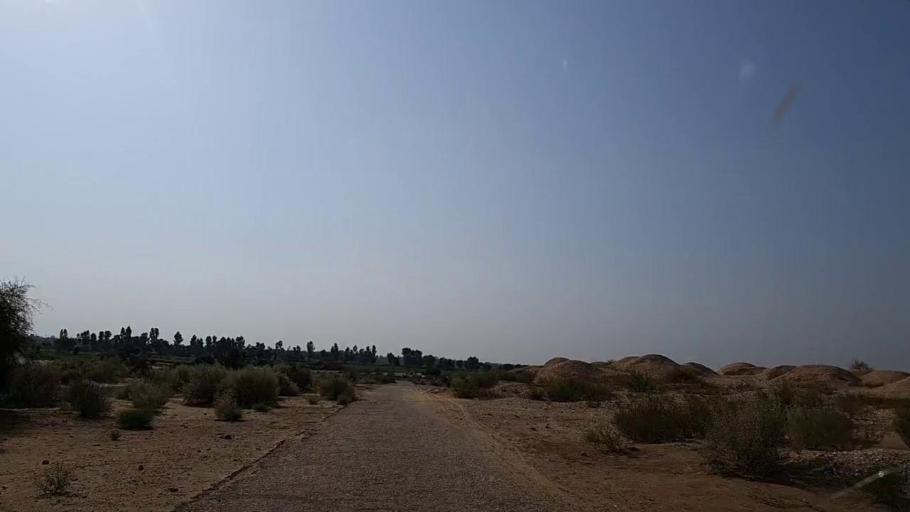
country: PK
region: Sindh
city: Khanpur
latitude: 27.7366
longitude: 69.3733
